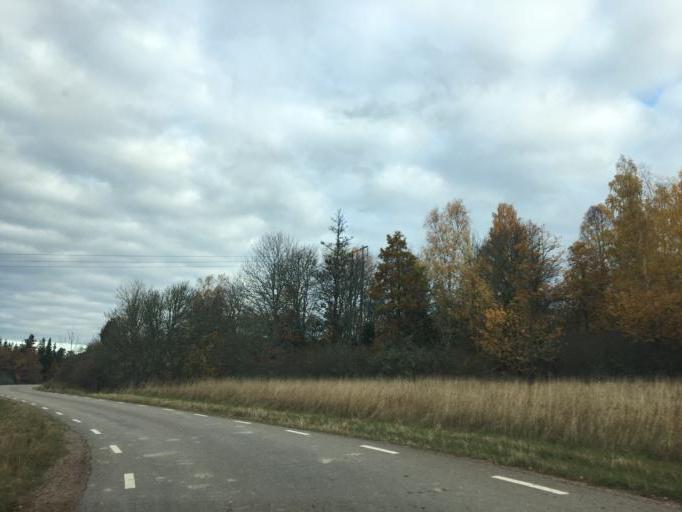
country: SE
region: Vaestmanland
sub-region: Vasteras
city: Vasteras
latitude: 59.5800
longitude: 16.4802
